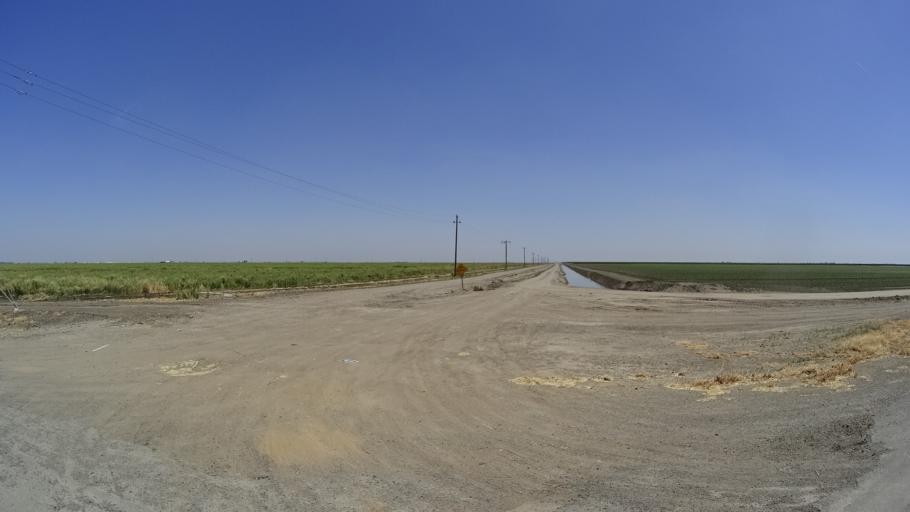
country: US
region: California
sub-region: Kings County
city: Corcoran
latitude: 36.1378
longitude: -119.6446
